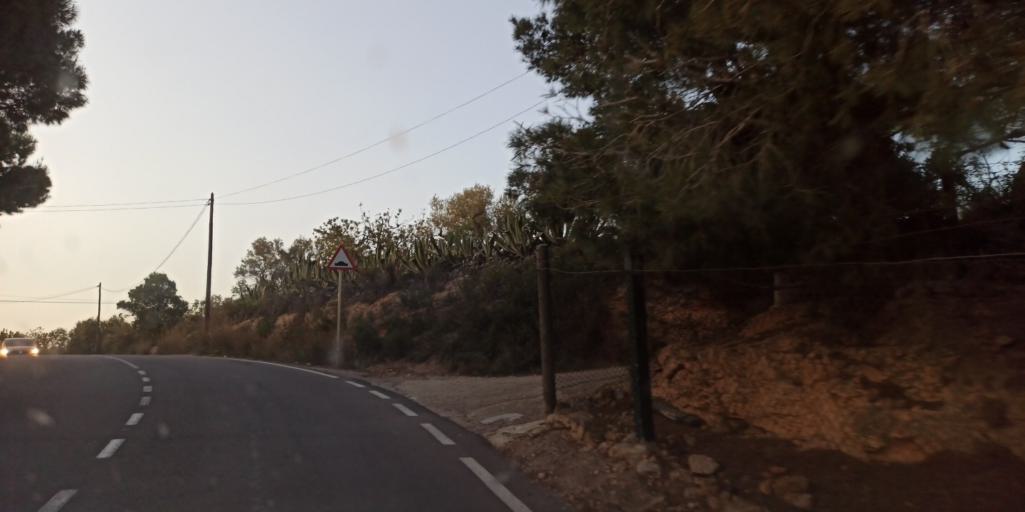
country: ES
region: Catalonia
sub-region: Provincia de Tarragona
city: L'Ampolla
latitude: 40.8174
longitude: 0.7210
